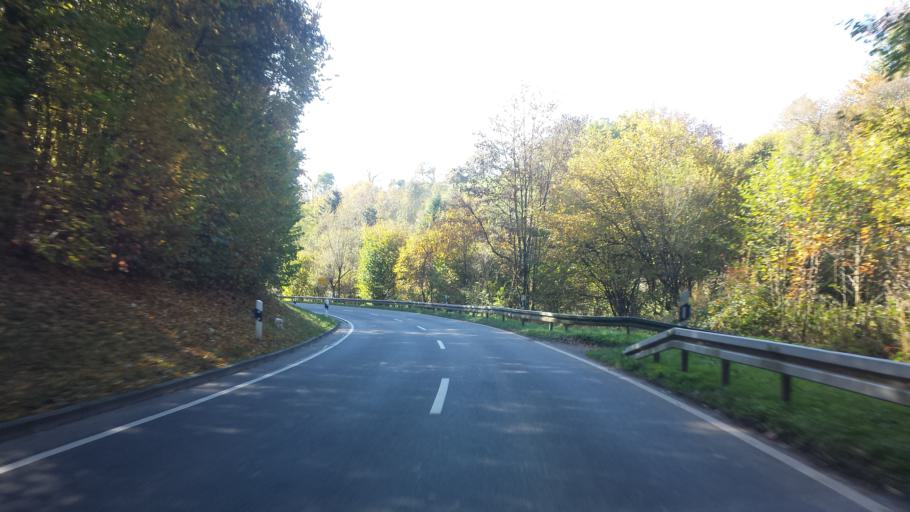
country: DE
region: Hesse
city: Zwingenberg
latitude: 49.7167
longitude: 8.6541
